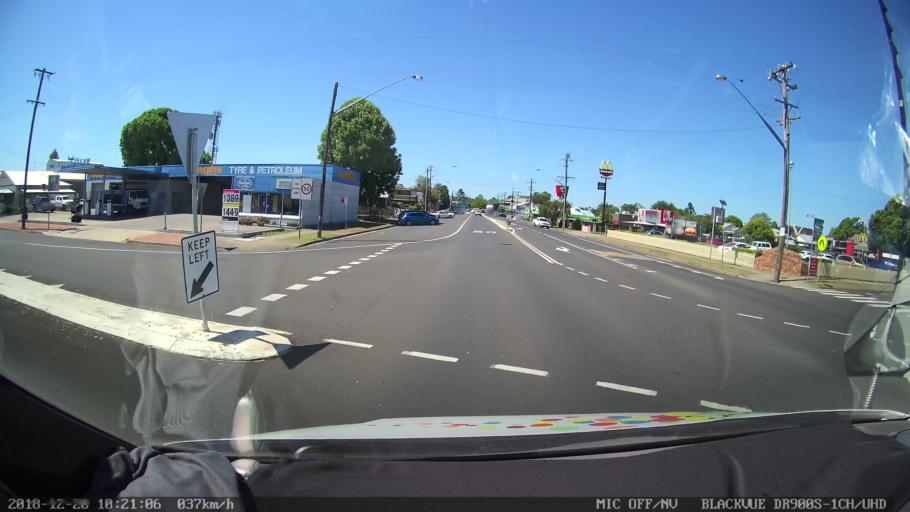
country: AU
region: New South Wales
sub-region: Richmond Valley
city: Casino
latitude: -28.8625
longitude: 153.0461
